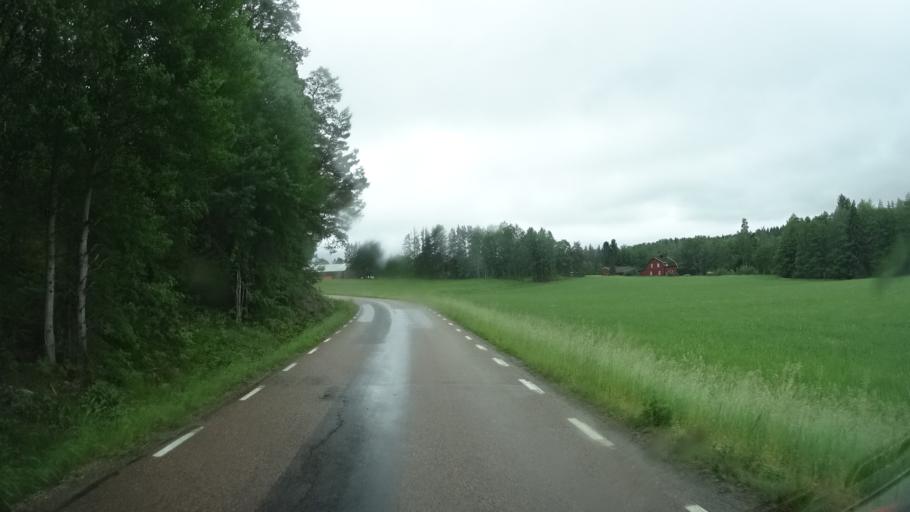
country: SE
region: Soedermanland
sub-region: Nykopings Kommun
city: Stigtomta
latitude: 58.7619
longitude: 16.7062
